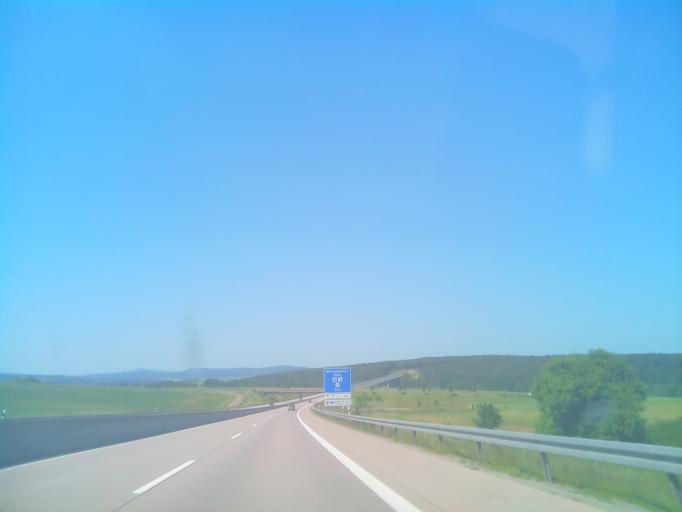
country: DE
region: Bavaria
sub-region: Regierungsbezirk Unterfranken
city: Hollstadt
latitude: 50.3793
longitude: 10.3127
